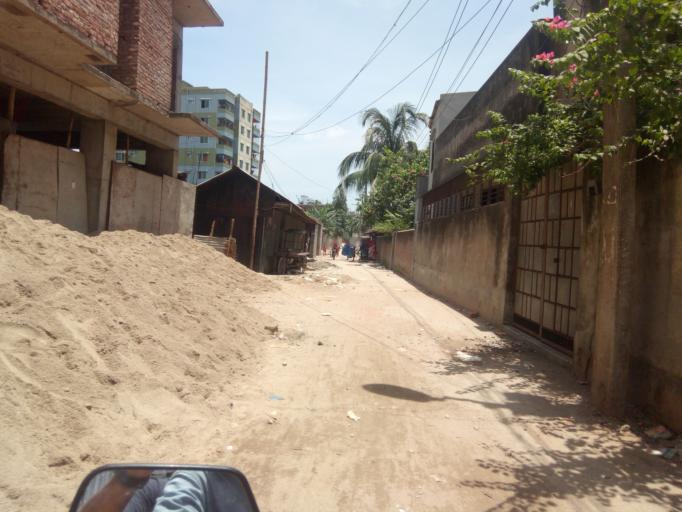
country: BD
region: Dhaka
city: Paltan
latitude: 23.7576
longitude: 90.4408
